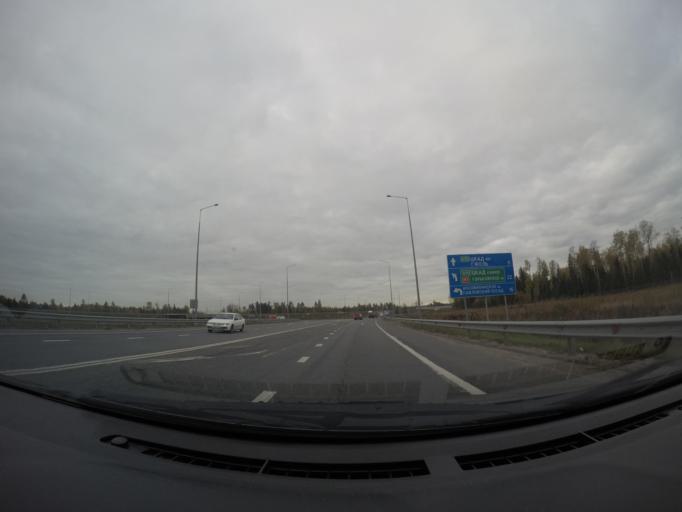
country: RU
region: Moskovskaya
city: Fryazevo
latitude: 55.6996
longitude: 38.4349
